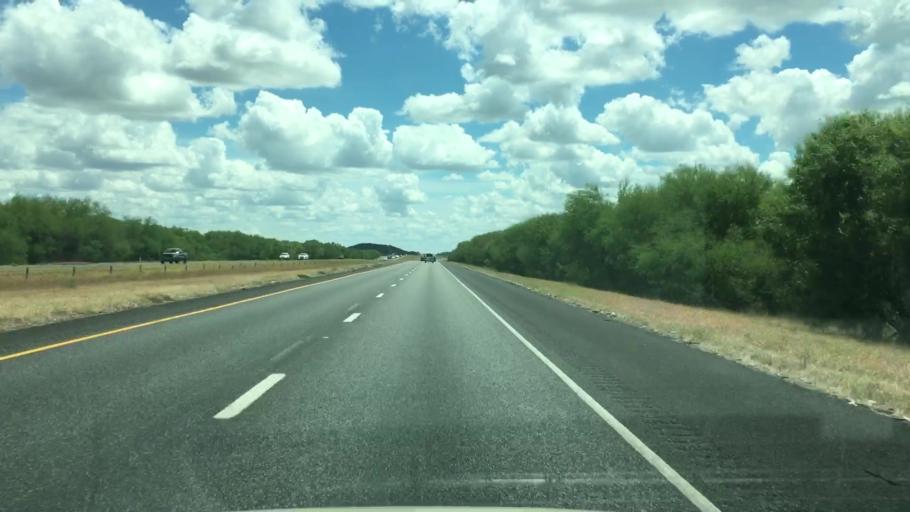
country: US
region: Texas
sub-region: Atascosa County
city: Pleasanton
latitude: 28.7437
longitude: -98.2929
